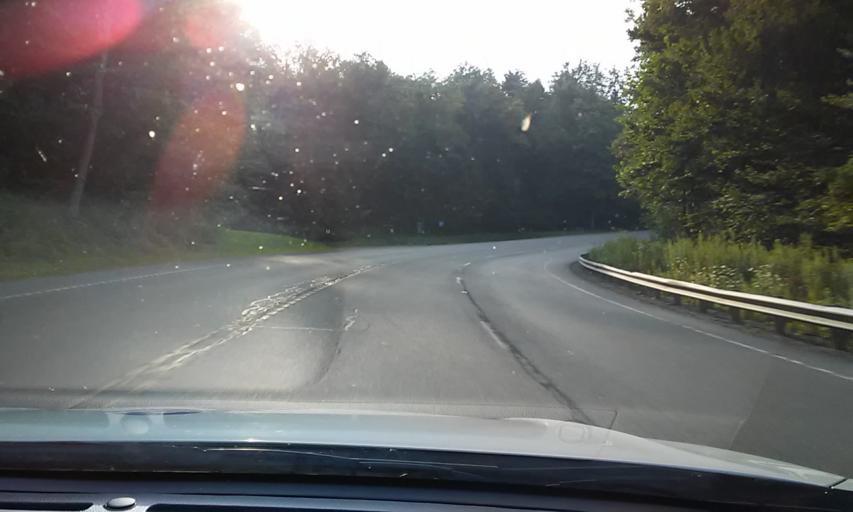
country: US
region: Pennsylvania
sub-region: McKean County
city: Smethport
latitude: 41.7180
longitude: -78.6099
